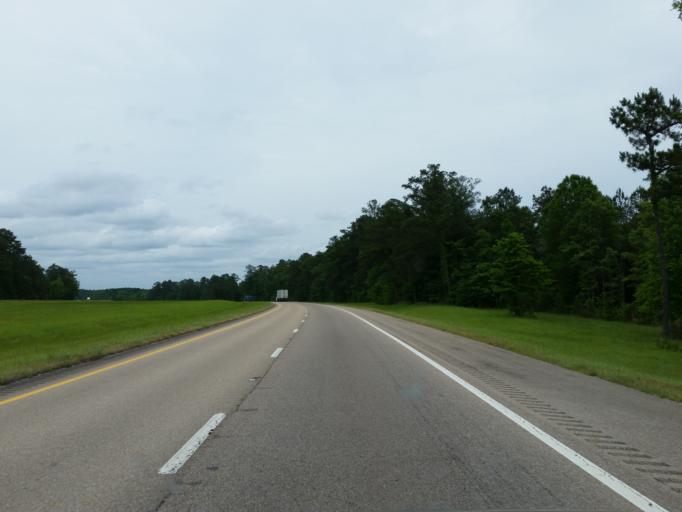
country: US
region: Mississippi
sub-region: Clarke County
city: Stonewall
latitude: 32.0149
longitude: -88.9251
